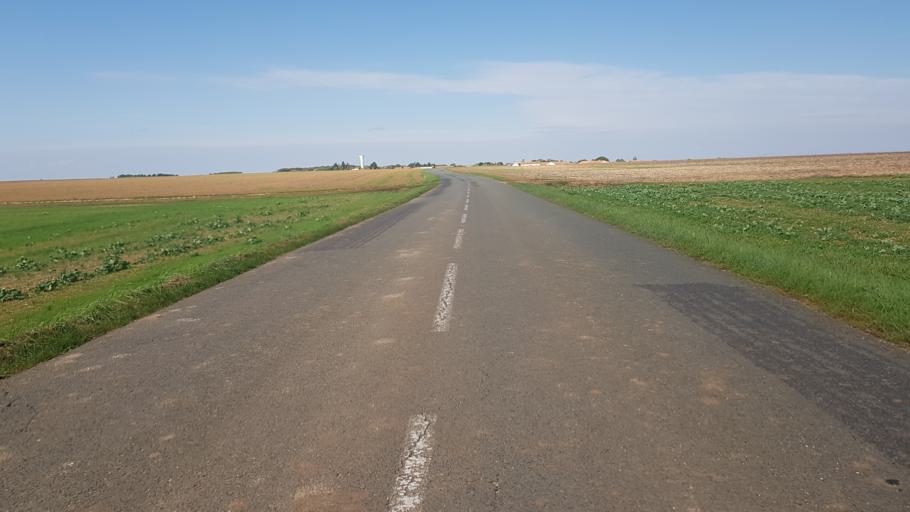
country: FR
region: Poitou-Charentes
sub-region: Departement de la Vienne
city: Chasseneuil-du-Poitou
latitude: 46.6529
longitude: 0.3431
